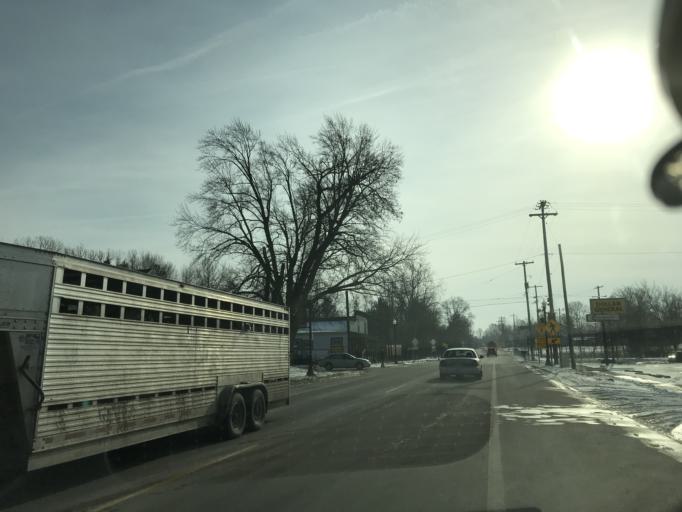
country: US
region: Michigan
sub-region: Barry County
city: Nashville
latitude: 42.6016
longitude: -85.0937
